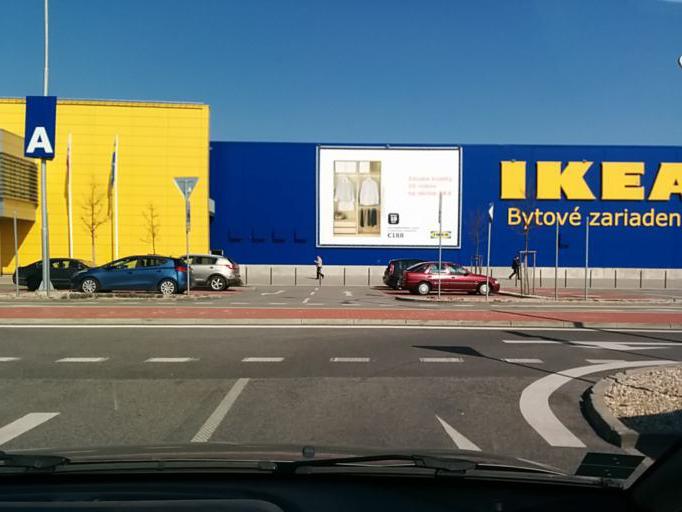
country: SK
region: Bratislavsky
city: Bratislava
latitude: 48.1675
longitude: 17.1824
